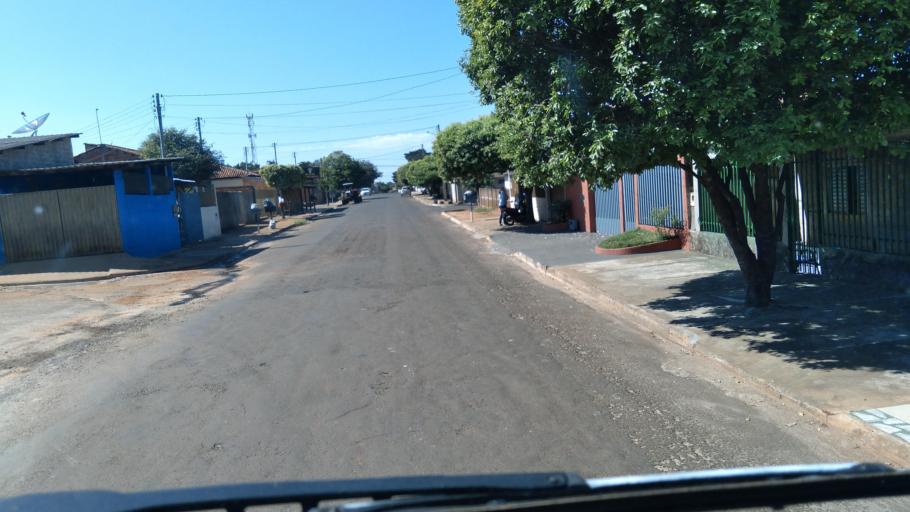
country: BR
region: Goias
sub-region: Mineiros
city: Mineiros
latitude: -17.5708
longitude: -52.5684
